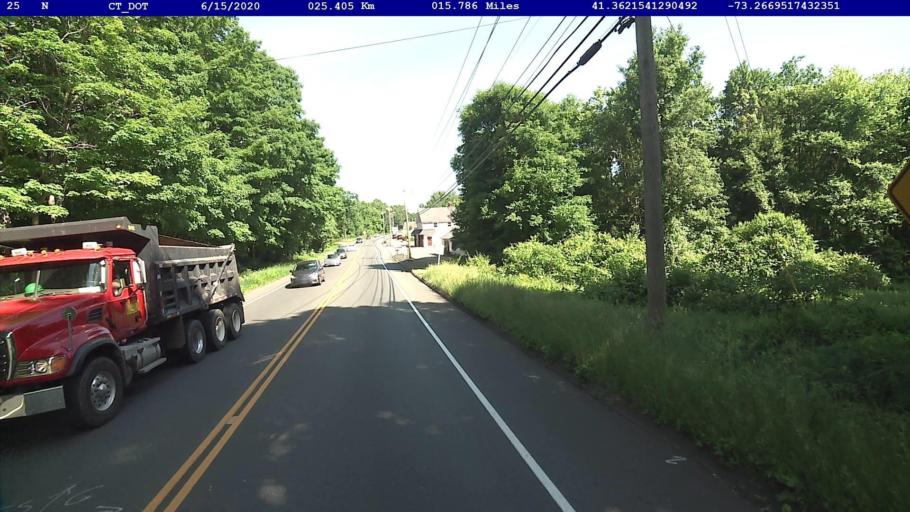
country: US
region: Connecticut
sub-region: Fairfield County
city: Newtown
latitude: 41.3622
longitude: -73.2670
